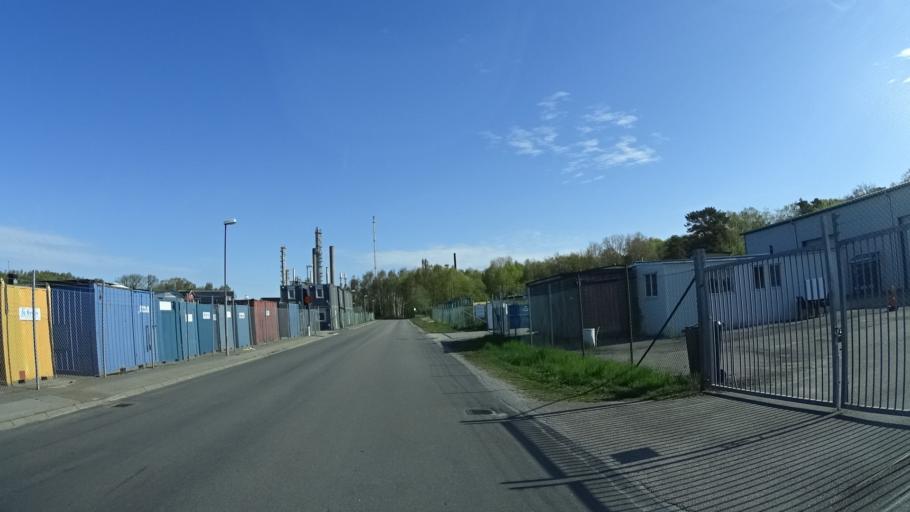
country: SE
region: Vaestra Goetaland
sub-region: Stenungsunds Kommun
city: Stenungsund
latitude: 58.0788
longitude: 11.8225
